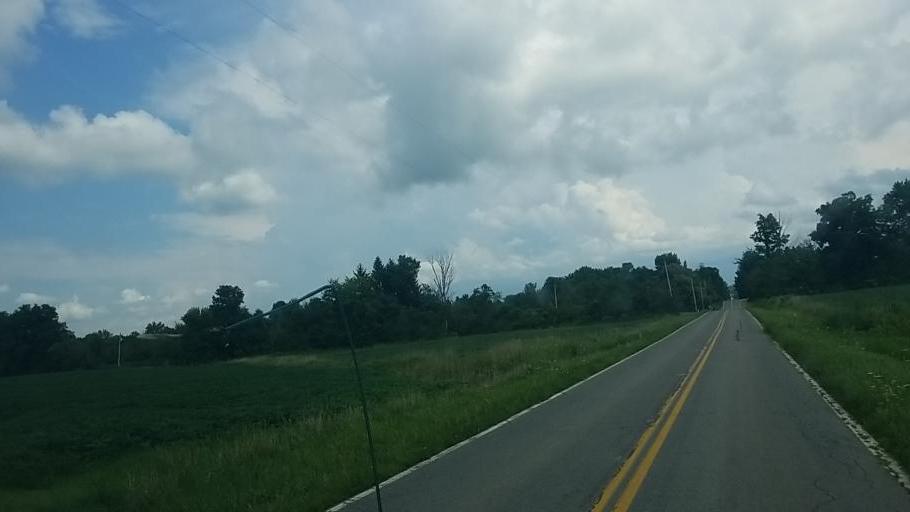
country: US
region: Ohio
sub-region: Medina County
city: Medina
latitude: 41.1423
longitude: -81.9608
